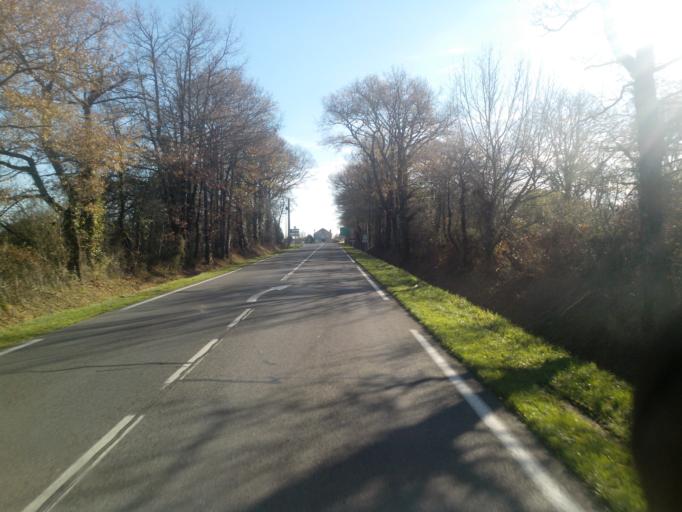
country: FR
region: Limousin
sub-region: Departement de la Haute-Vienne
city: Bussiere-Poitevine
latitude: 46.2431
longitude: 0.8900
